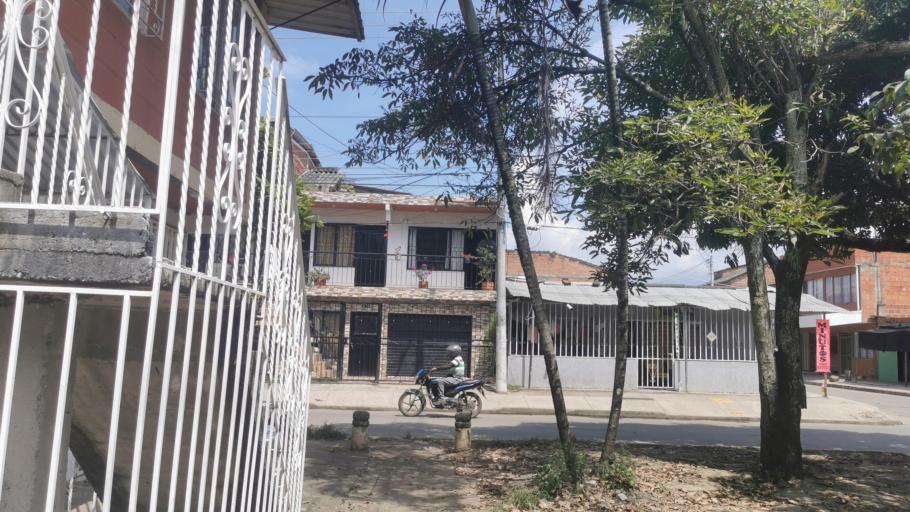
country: CO
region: Valle del Cauca
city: Jamundi
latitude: 3.2554
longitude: -76.5392
